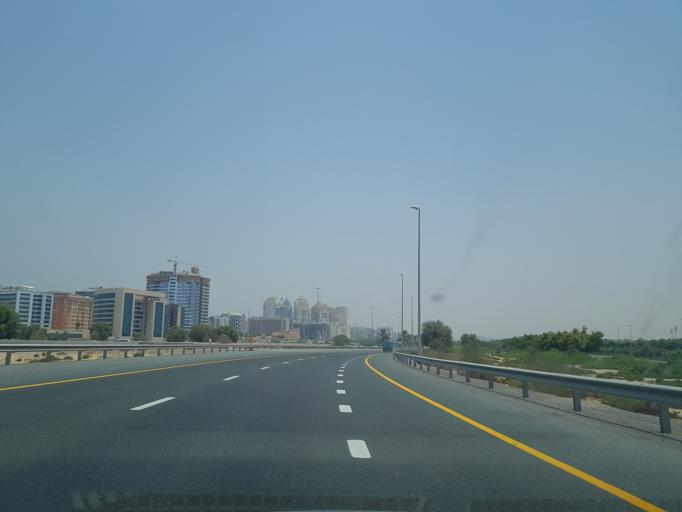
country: AE
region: Dubai
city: Dubai
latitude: 25.1053
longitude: 55.3820
